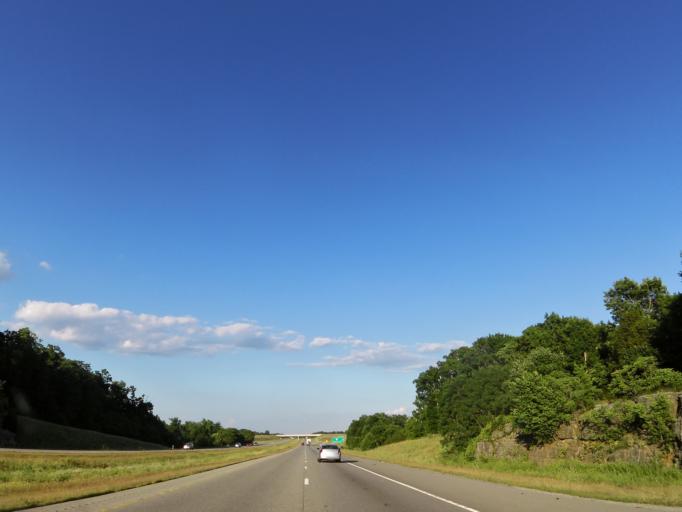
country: US
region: Tennessee
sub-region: Williamson County
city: Nolensville
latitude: 35.8577
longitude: -86.5903
